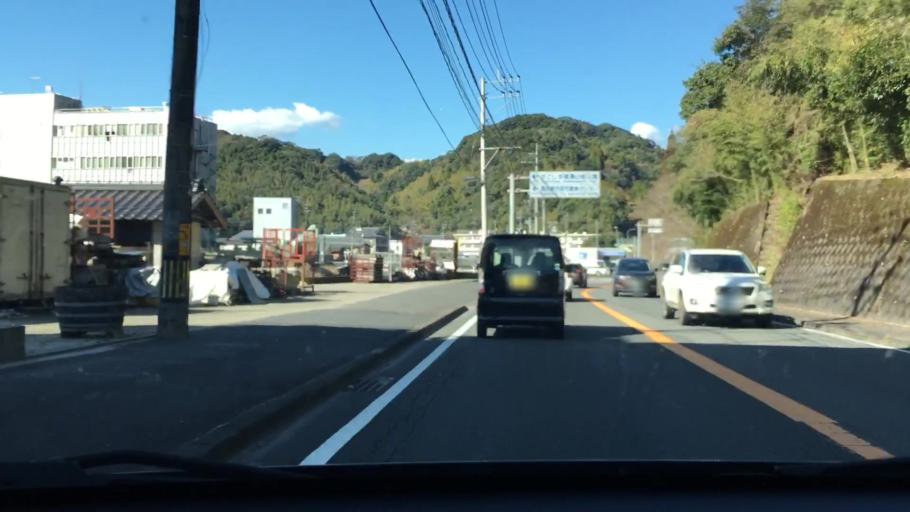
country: JP
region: Kagoshima
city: Kagoshima-shi
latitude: 31.6404
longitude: 130.5161
